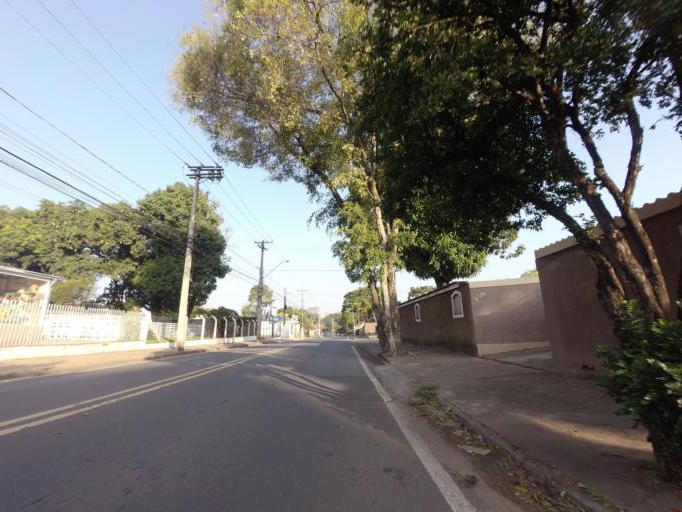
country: BR
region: Sao Paulo
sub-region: Piracicaba
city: Piracicaba
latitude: -22.7414
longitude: -47.6056
